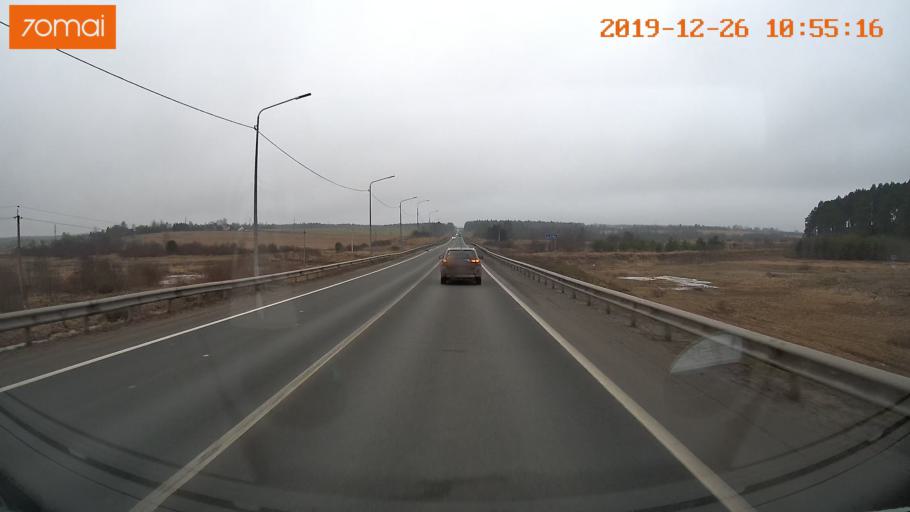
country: RU
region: Vologda
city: Molochnoye
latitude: 59.1881
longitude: 39.5854
